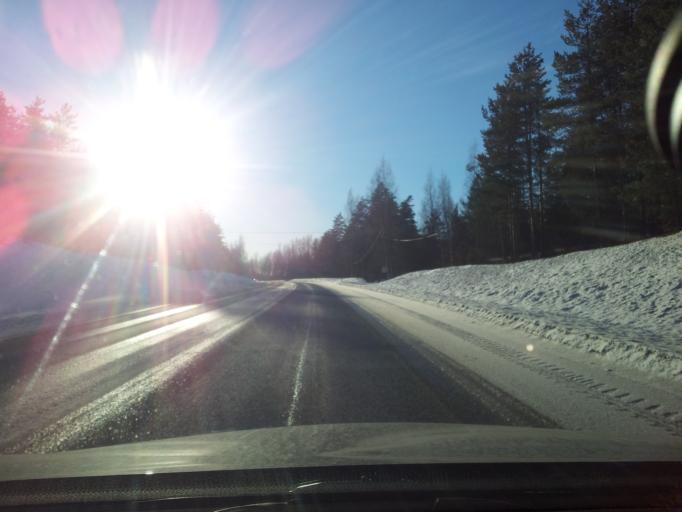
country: FI
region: Uusimaa
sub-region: Helsinki
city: Vihti
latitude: 60.3585
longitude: 24.3428
